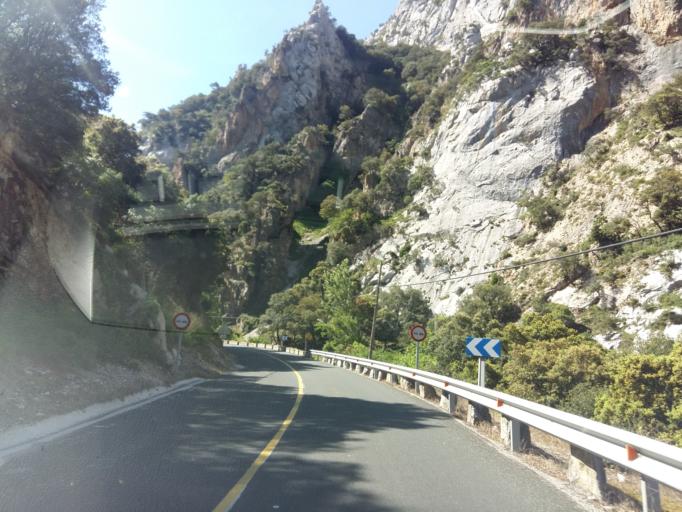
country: ES
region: Cantabria
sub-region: Provincia de Cantabria
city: Potes
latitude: 43.2044
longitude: -4.5936
